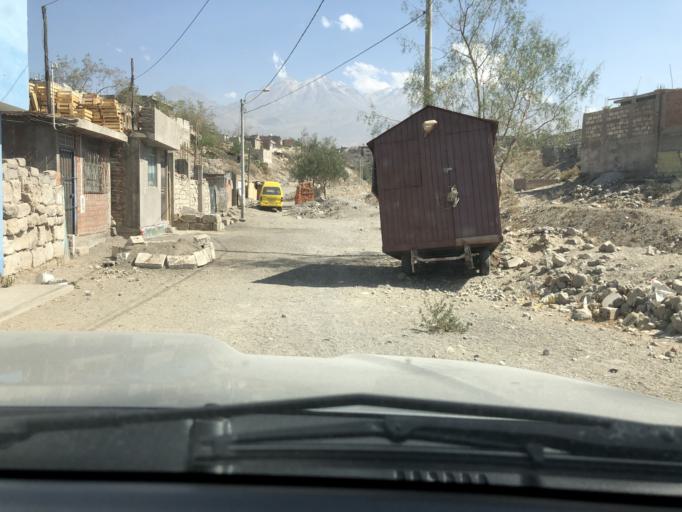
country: PE
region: Arequipa
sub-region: Provincia de Arequipa
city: Arequipa
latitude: -16.3426
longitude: -71.5503
